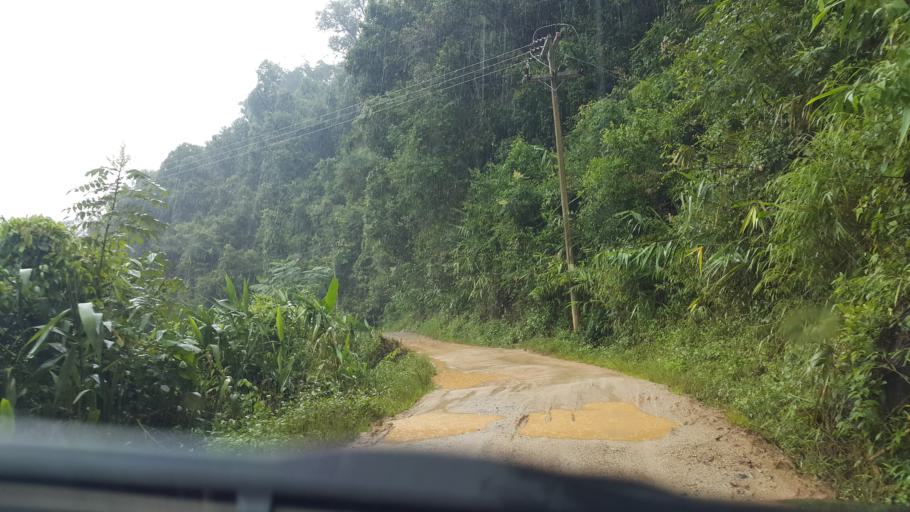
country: TH
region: Chiang Rai
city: Wiang Pa Pao
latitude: 19.1316
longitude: 99.3513
